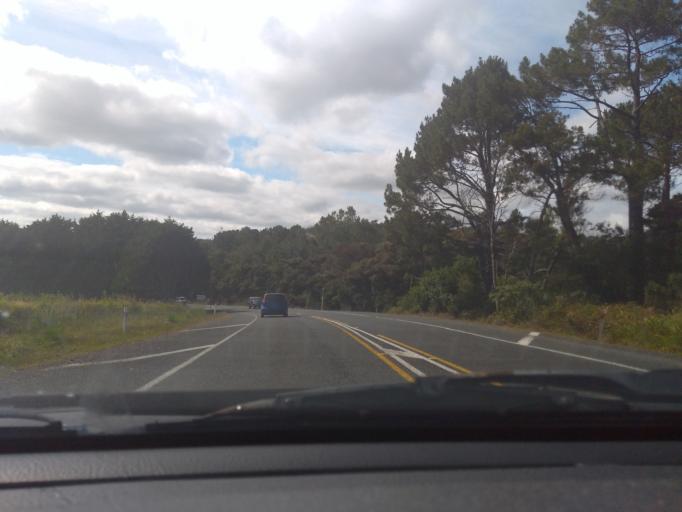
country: NZ
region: Northland
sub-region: Far North District
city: Taipa
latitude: -34.9920
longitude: 173.5236
